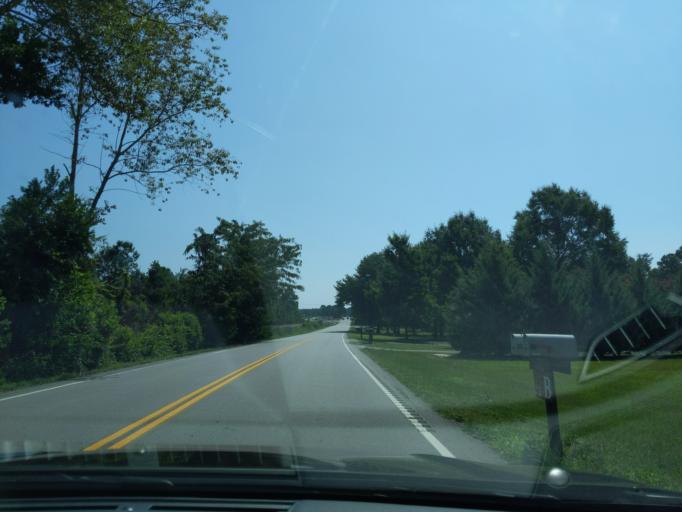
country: US
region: South Carolina
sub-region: Lexington County
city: Red Bank
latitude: 33.9305
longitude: -81.3170
